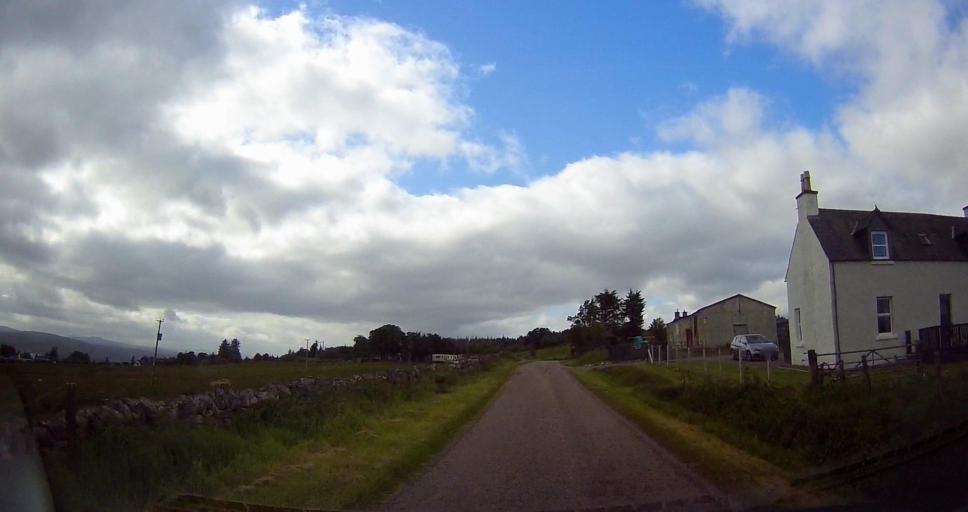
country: GB
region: Scotland
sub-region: Highland
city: Alness
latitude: 58.0789
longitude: -4.4461
